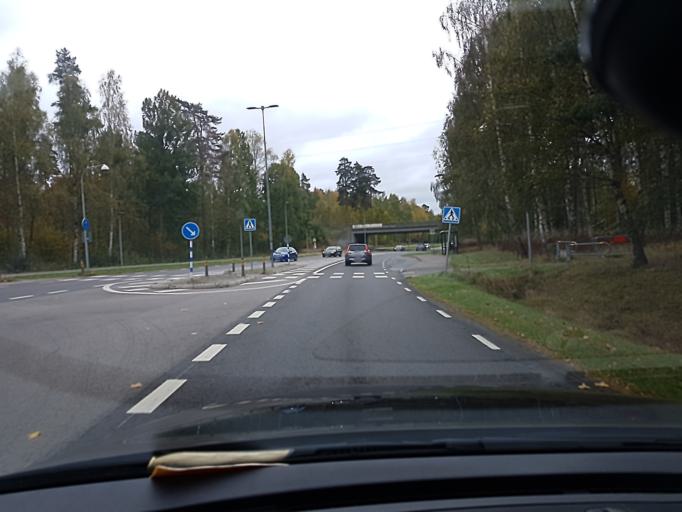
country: SE
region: Kronoberg
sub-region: Vaxjo Kommun
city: Vaexjoe
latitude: 56.9023
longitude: 14.7979
